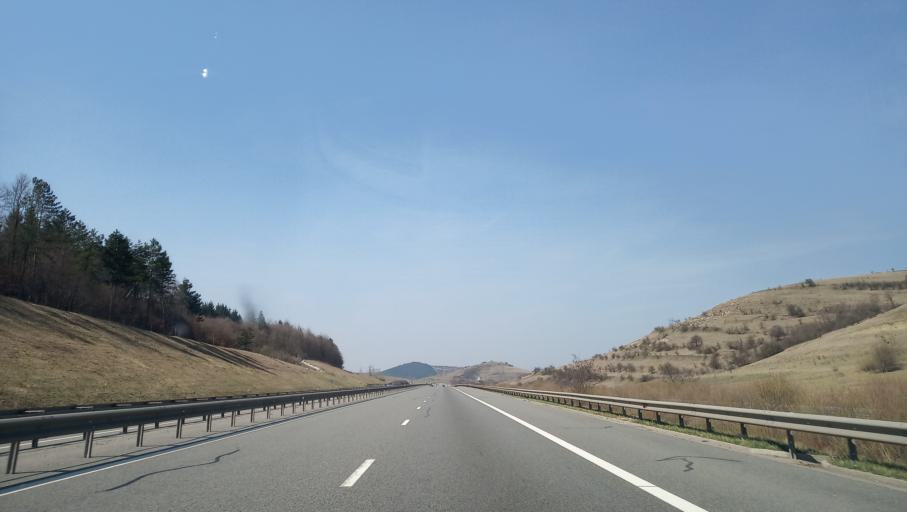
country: RO
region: Cluj
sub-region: Comuna Savadisla
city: Savadisla
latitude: 46.6781
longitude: 23.4771
